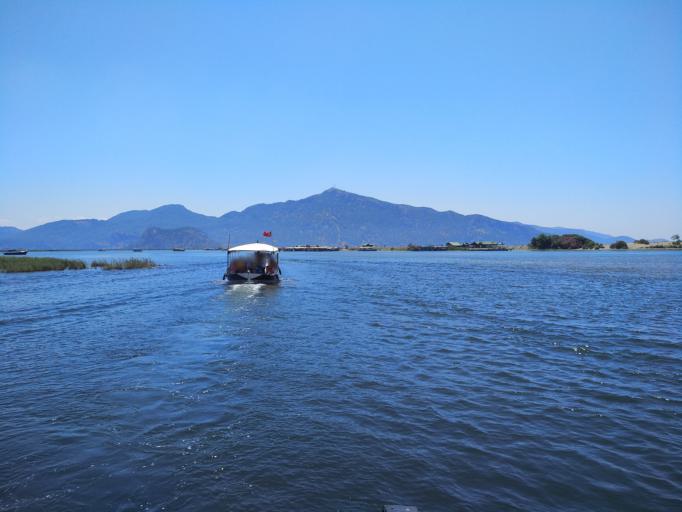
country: TR
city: Dalyan
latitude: 36.8043
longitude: 28.6045
